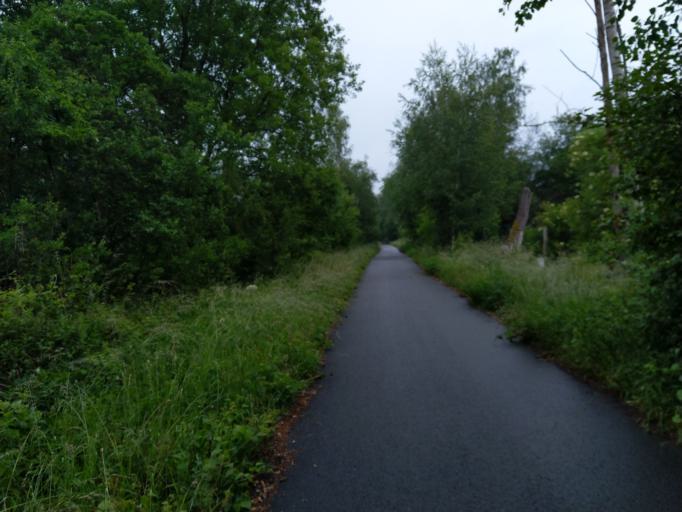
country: BE
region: Wallonia
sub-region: Province de Namur
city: Anhee
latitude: 50.3182
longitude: 4.8490
